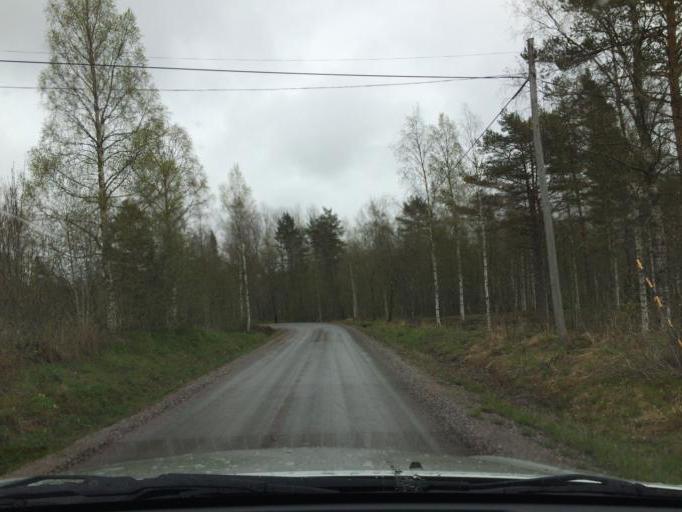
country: SE
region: Dalarna
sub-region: Ludvika Kommun
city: Abborrberget
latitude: 60.0407
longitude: 14.6973
